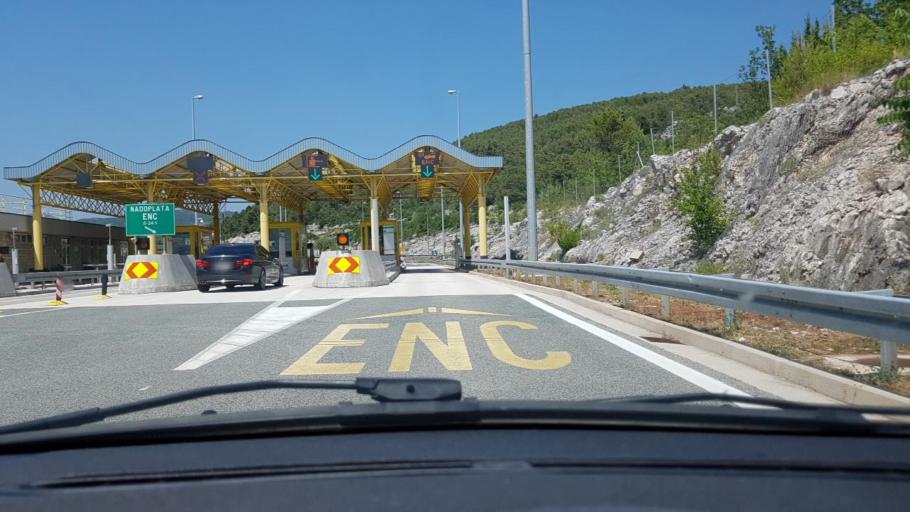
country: HR
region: Splitsko-Dalmatinska
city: Vrgorac
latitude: 43.1912
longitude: 17.3791
